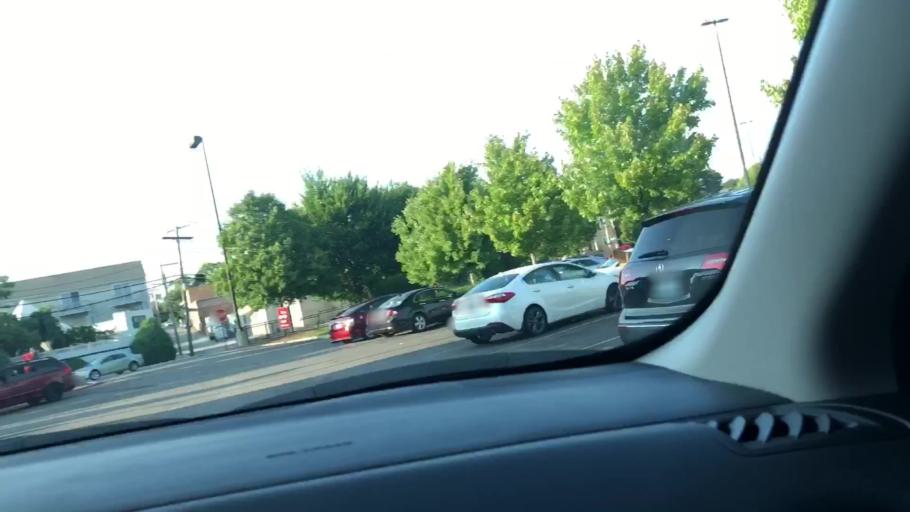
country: US
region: Rhode Island
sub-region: Providence County
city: Providence
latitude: 41.8447
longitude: -71.4181
